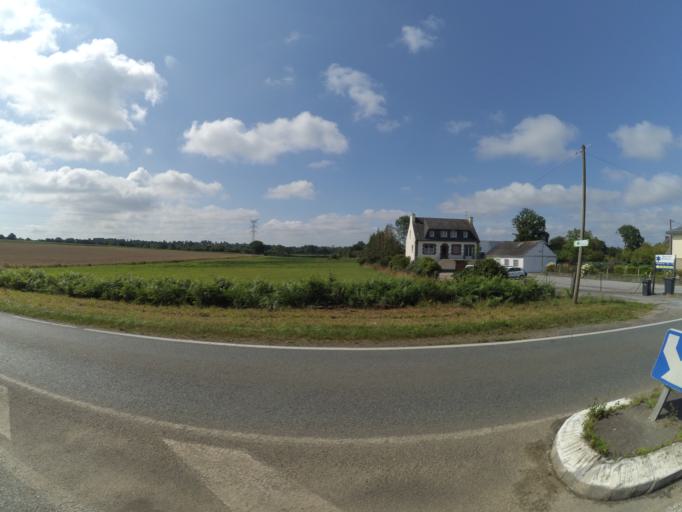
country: FR
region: Brittany
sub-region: Departement du Finistere
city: Rosporden
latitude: 47.9509
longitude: -3.7828
